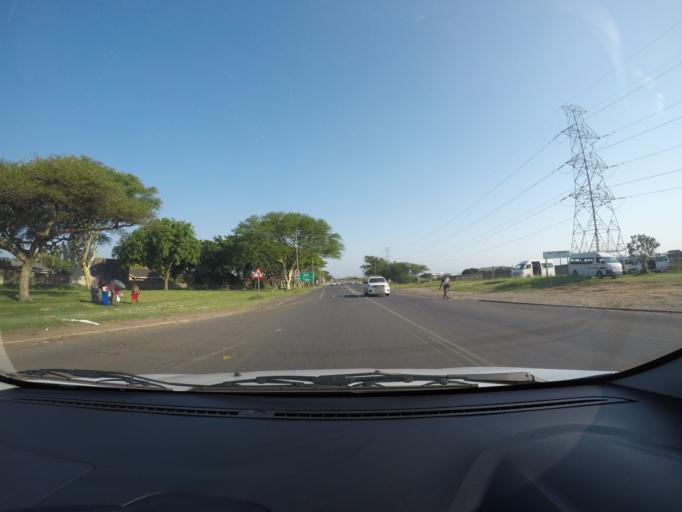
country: ZA
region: KwaZulu-Natal
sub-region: uThungulu District Municipality
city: Richards Bay
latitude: -28.7296
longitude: 32.0377
